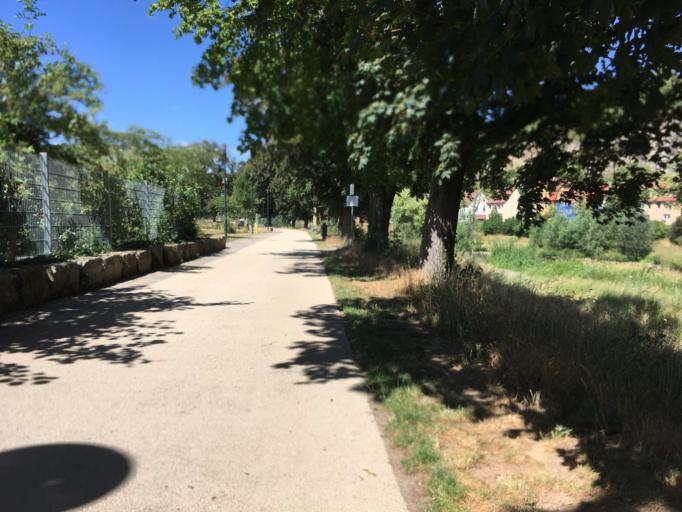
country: DE
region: Baden-Wuerttemberg
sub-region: Karlsruhe Region
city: Muhlacker
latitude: 48.9418
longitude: 8.8431
